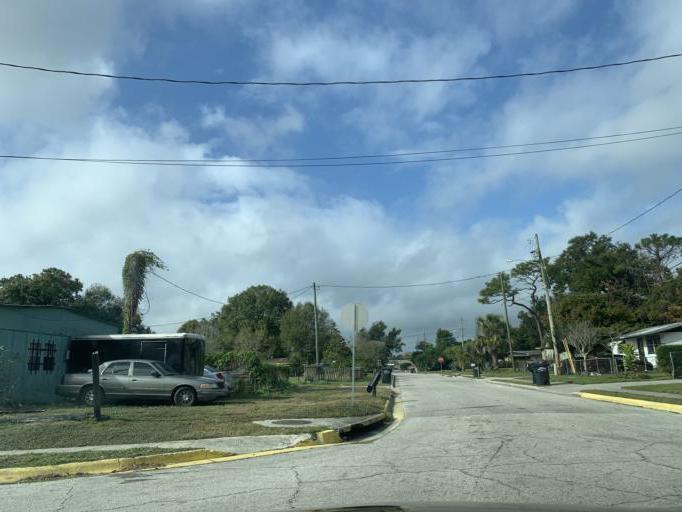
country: US
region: Florida
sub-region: Orange County
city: Eatonville
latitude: 28.6195
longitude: -81.3819
